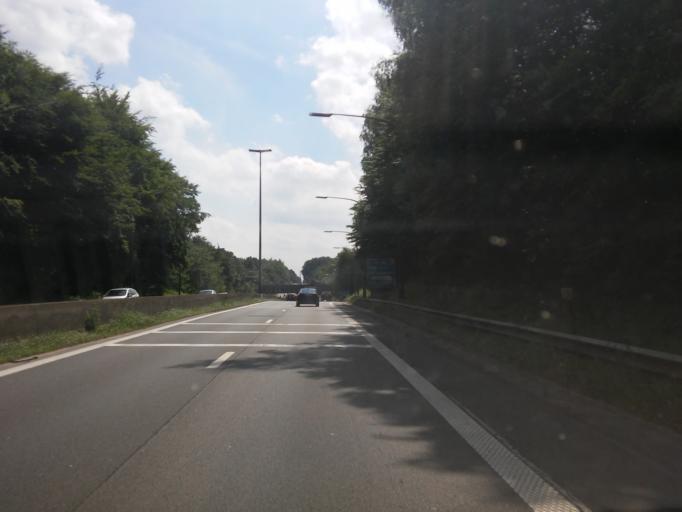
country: BE
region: Flanders
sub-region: Provincie Vlaams-Brabant
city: Hoeilaart
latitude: 50.7717
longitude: 4.4456
